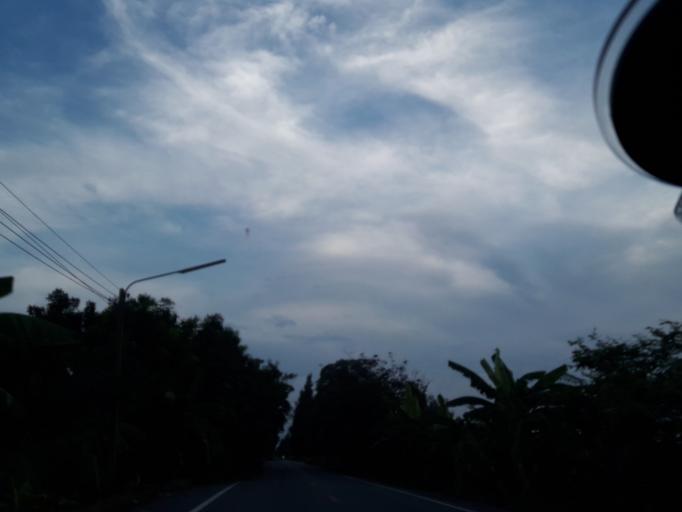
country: TH
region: Pathum Thani
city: Nong Suea
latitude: 14.1725
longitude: 100.8689
